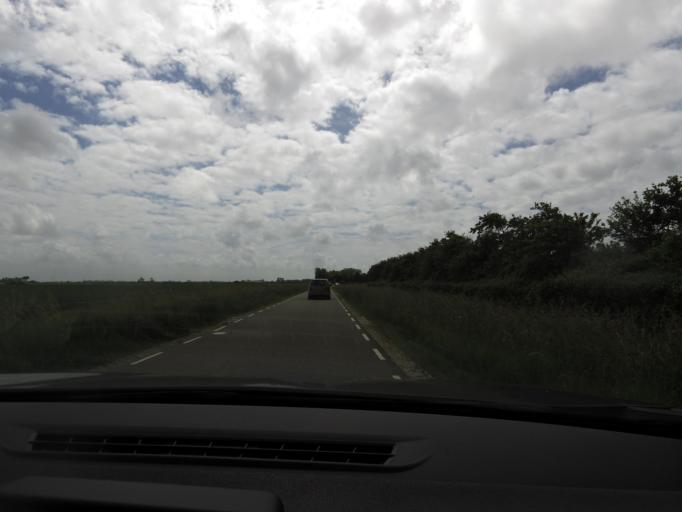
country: NL
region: Zeeland
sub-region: Schouwen-Duiveland
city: Renesse
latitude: 51.7367
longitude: 3.7993
